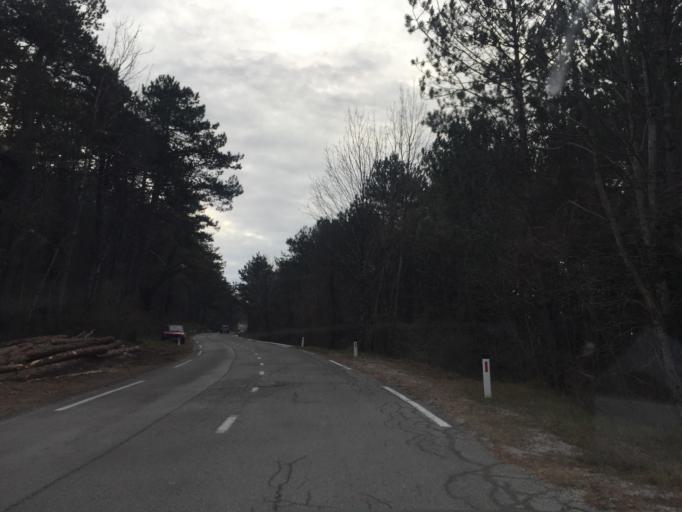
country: SI
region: Nova Gorica
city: Sempas
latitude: 45.9761
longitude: 13.7178
